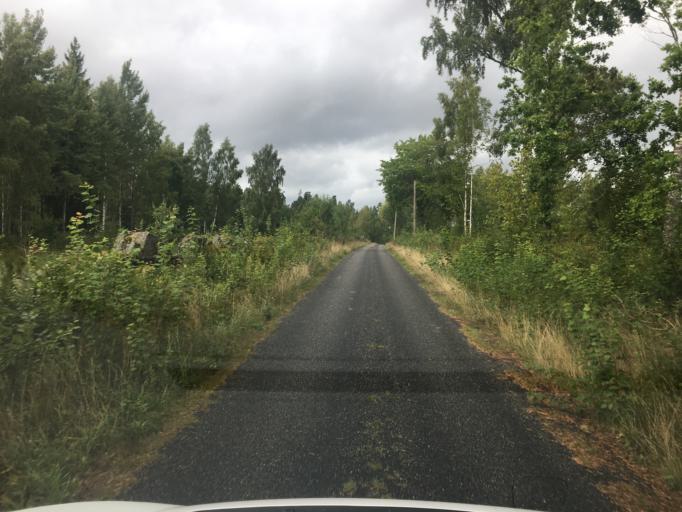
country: SE
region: Kronoberg
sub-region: Ljungby Kommun
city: Lagan
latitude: 56.9351
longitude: 14.0252
